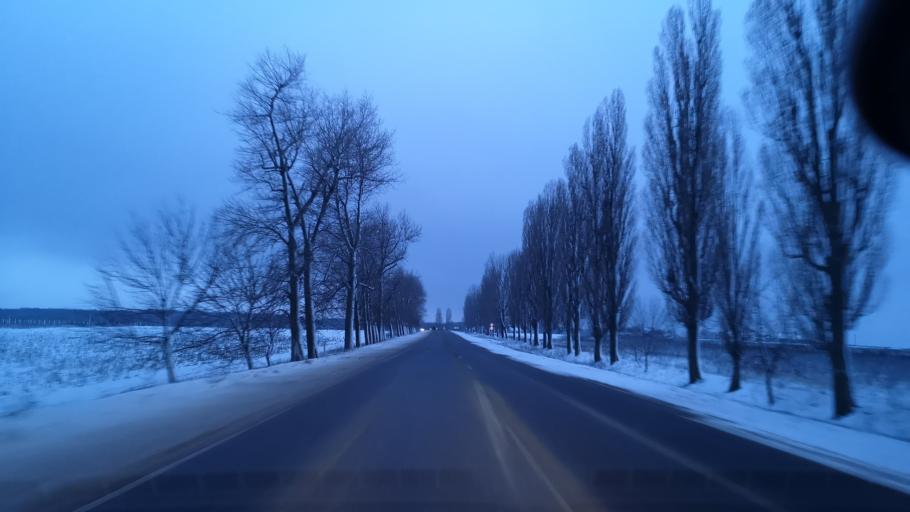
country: MD
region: Rezina
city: Rezina
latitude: 47.7370
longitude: 28.8831
